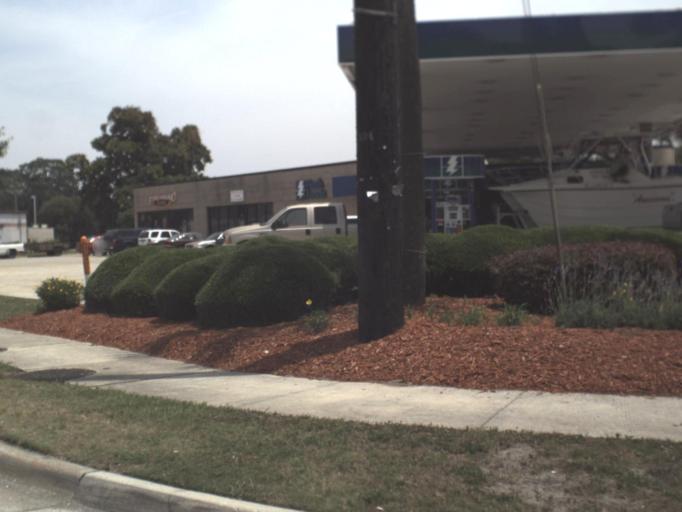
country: US
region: Florida
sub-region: Nassau County
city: Fernandina Beach
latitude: 30.6394
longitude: -81.4584
